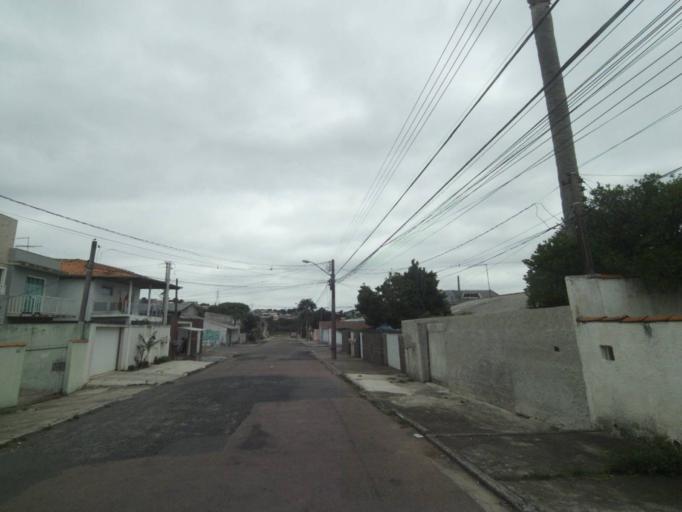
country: BR
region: Parana
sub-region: Sao Jose Dos Pinhais
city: Sao Jose dos Pinhais
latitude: -25.5330
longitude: -49.2574
